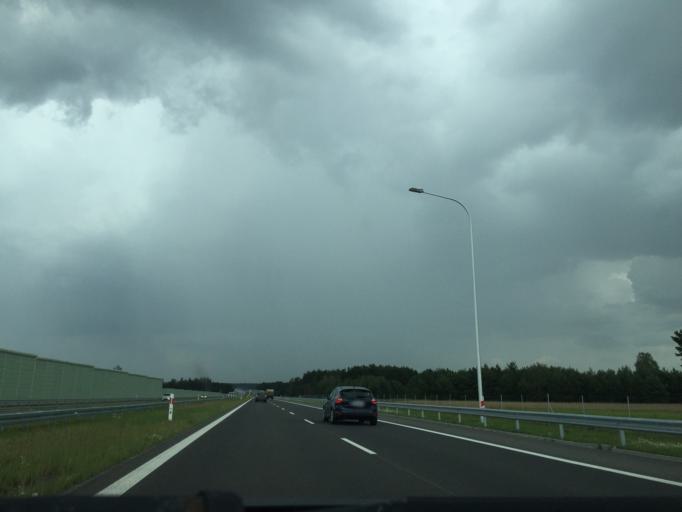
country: PL
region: Masovian Voivodeship
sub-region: Powiat szydlowiecki
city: Oronsko
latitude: 51.3035
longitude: 20.9998
